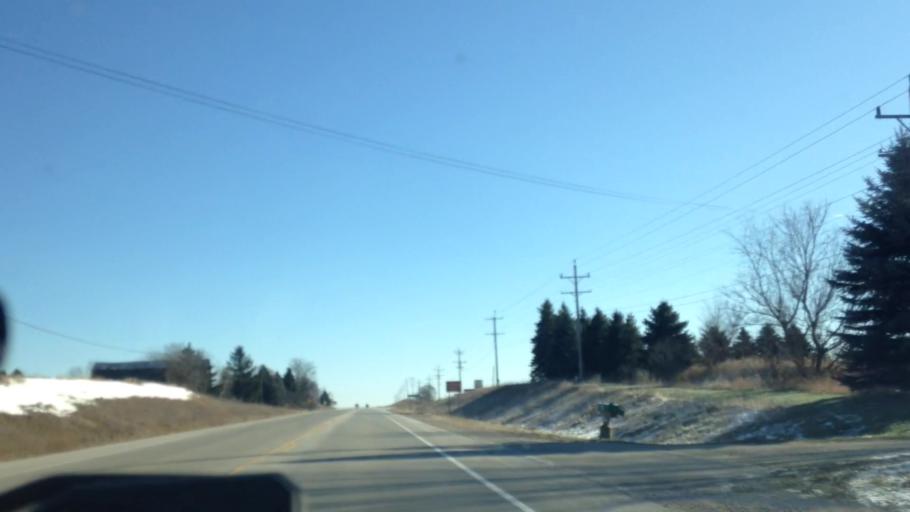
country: US
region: Wisconsin
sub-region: Washington County
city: West Bend
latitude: 43.4274
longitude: -88.2749
